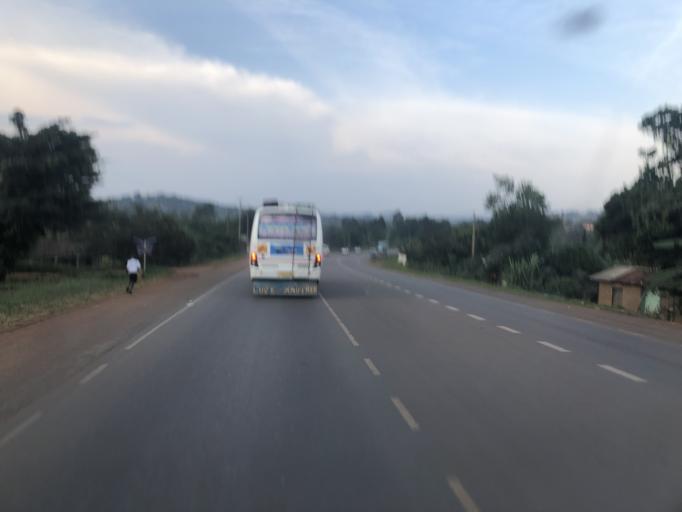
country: UG
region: Central Region
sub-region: Mpigi District
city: Mpigi
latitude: 0.2472
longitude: 32.3836
